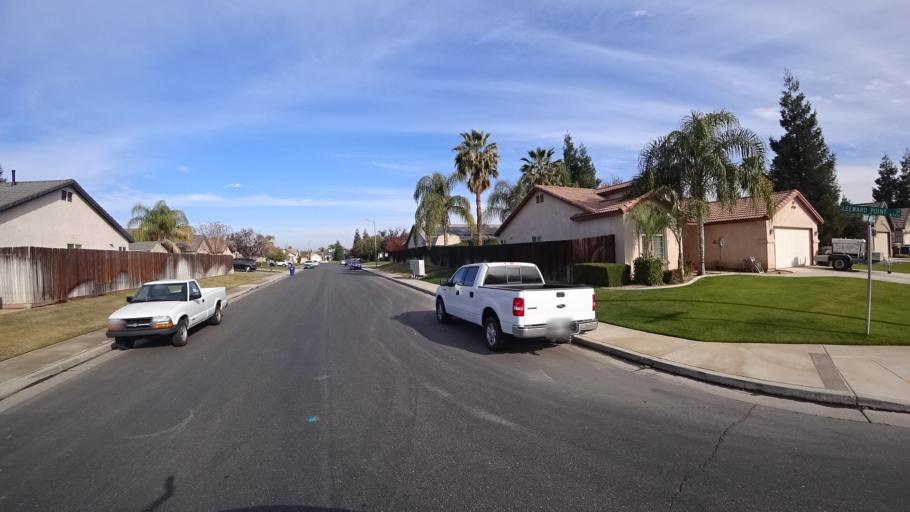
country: US
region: California
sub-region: Kern County
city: Rosedale
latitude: 35.4093
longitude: -119.1295
